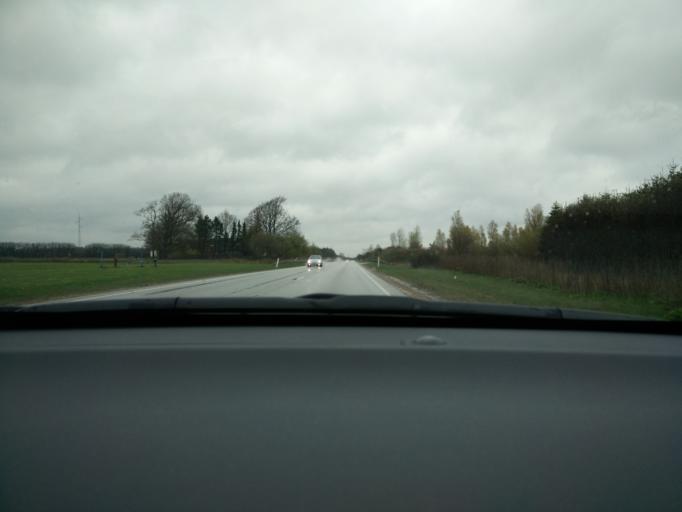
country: DK
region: Central Jutland
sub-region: Viborg Kommune
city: Viborg
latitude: 56.4648
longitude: 9.3750
